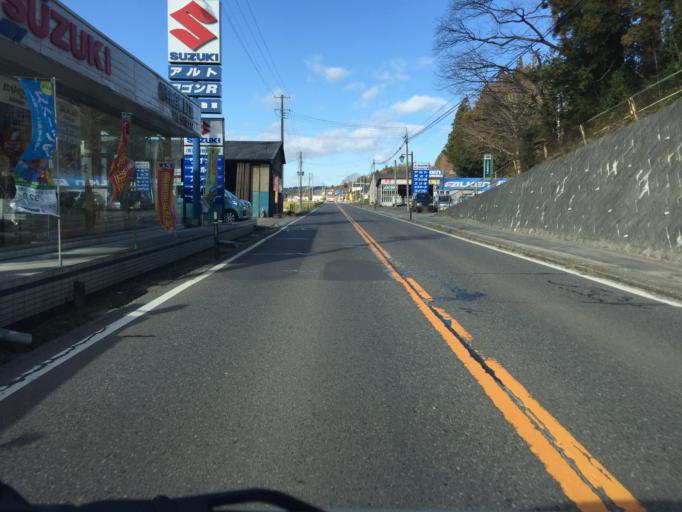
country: JP
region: Fukushima
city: Ishikawa
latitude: 37.2522
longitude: 140.5602
